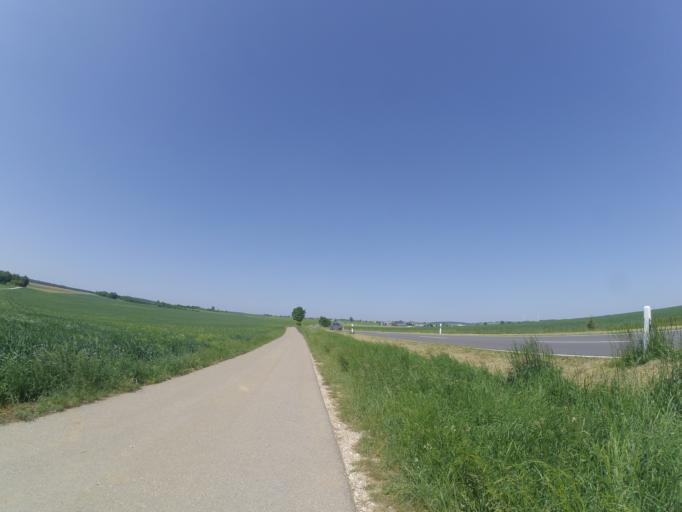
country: DE
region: Baden-Wuerttemberg
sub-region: Tuebingen Region
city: Merklingen
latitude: 48.5259
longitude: 9.7728
